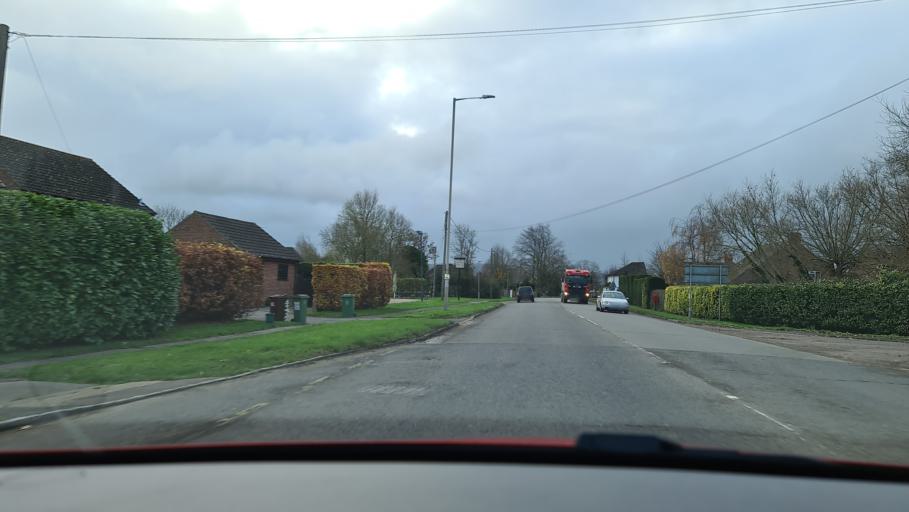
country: GB
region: England
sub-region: Buckinghamshire
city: Weston Turville
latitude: 51.7853
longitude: -0.7908
